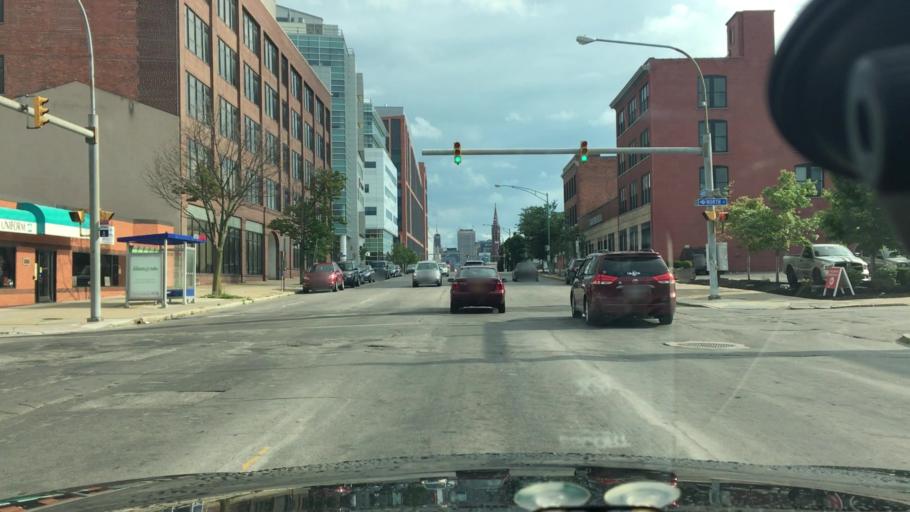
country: US
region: New York
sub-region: Erie County
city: Buffalo
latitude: 42.9023
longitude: -78.8690
